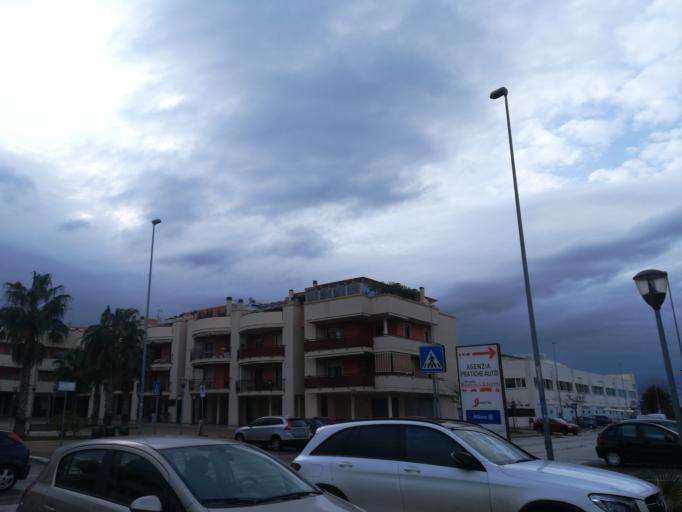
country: IT
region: Apulia
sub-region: Provincia di Bari
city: Polignano a Mare
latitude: 40.9934
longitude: 17.2125
